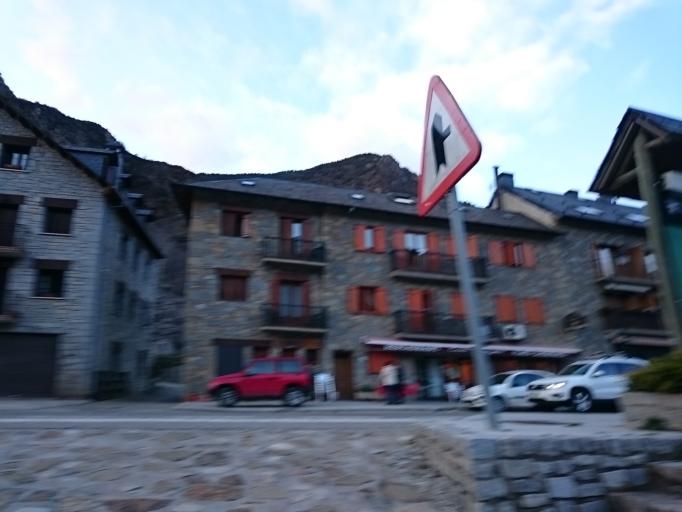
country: ES
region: Aragon
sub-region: Provincia de Huesca
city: Bonansa
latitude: 42.5042
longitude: 0.8013
